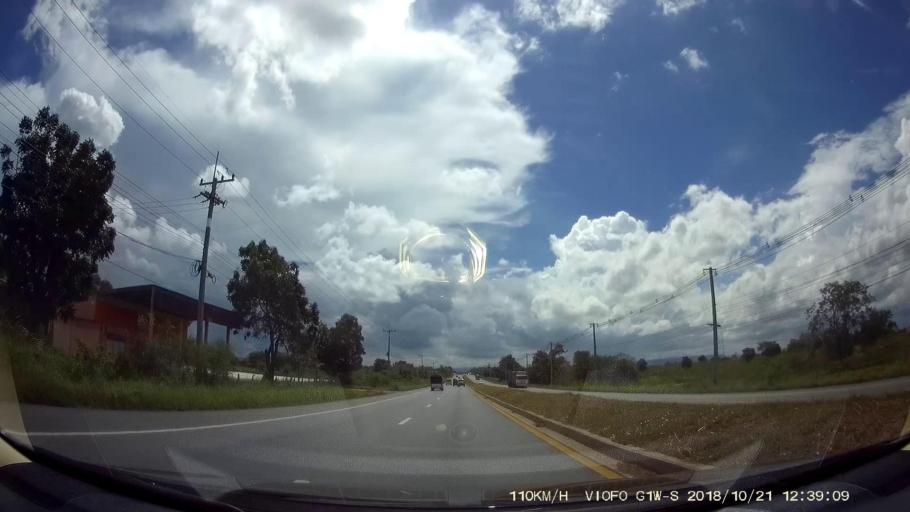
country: TH
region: Nakhon Ratchasima
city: Amphoe Sikhiu
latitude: 15.0427
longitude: 101.7021
